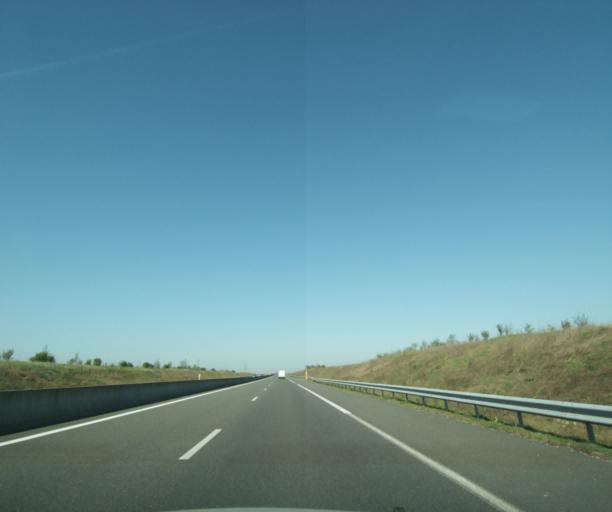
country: FR
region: Centre
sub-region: Departement du Loiret
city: Beaune-la-Rolande
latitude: 48.0958
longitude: 2.4037
